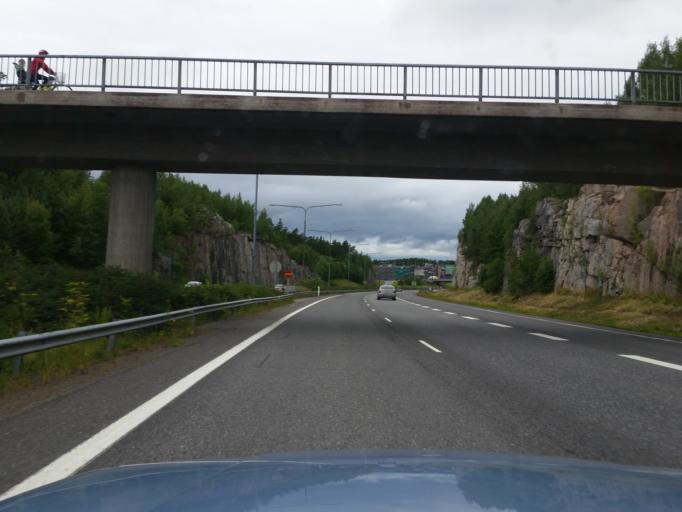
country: FI
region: Varsinais-Suomi
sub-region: Turku
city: Kaarina
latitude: 60.4250
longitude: 22.3350
